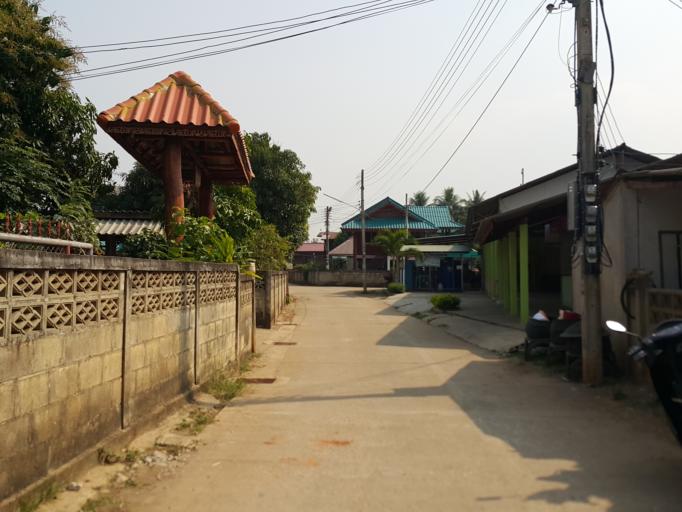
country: TH
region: Sukhothai
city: Thung Saliam
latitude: 17.3252
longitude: 99.5204
